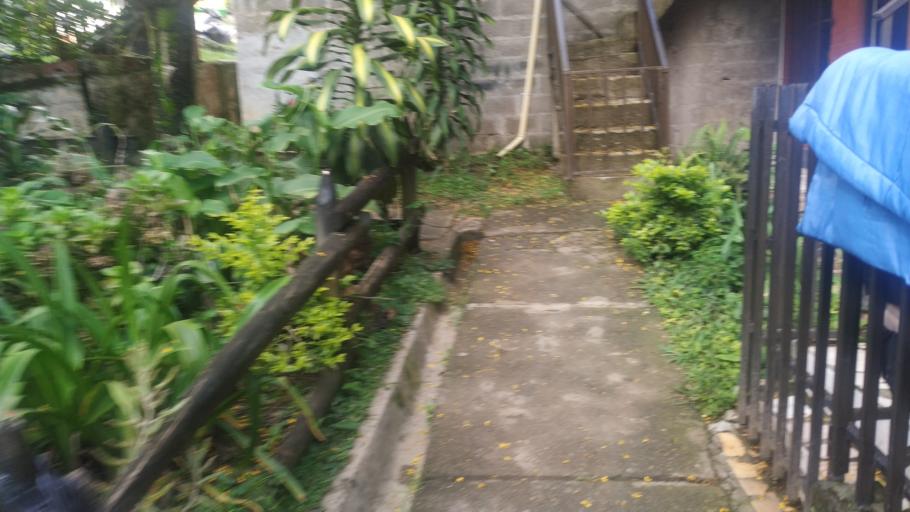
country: CO
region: Antioquia
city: Medellin
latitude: 6.2266
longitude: -75.5424
